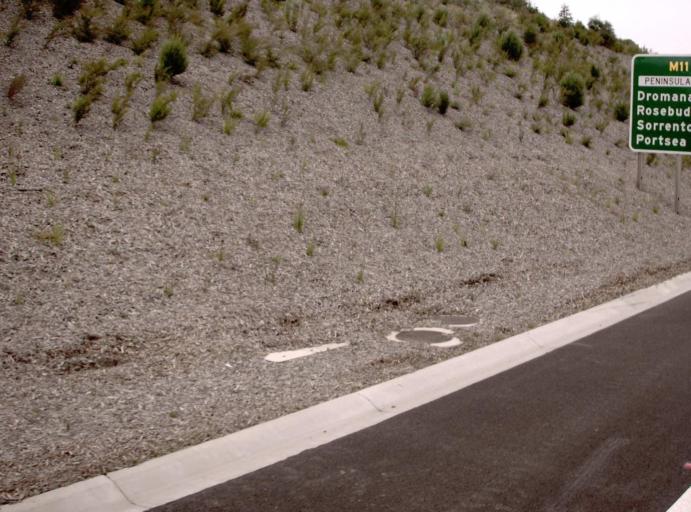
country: AU
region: Victoria
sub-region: Frankston
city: Langwarrin
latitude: -38.1649
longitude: 145.1652
